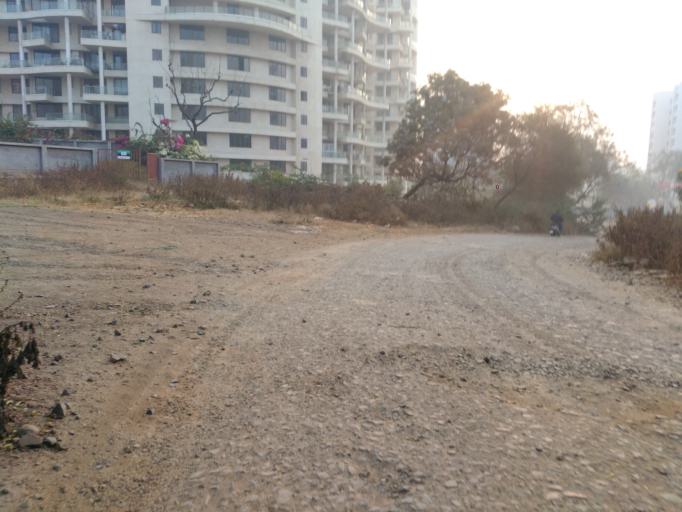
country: IN
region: Maharashtra
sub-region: Pune Division
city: Pune
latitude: 18.4604
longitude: 73.9017
